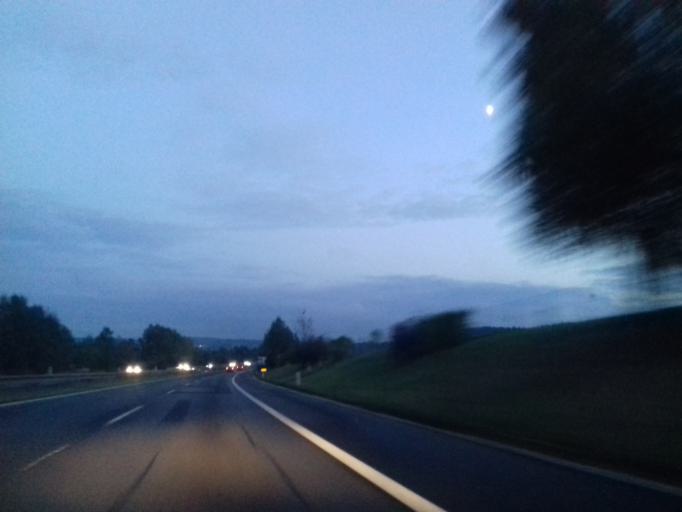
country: CZ
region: Vysocina
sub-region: Okres Pelhrimov
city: Humpolec
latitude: 49.5543
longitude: 15.3247
